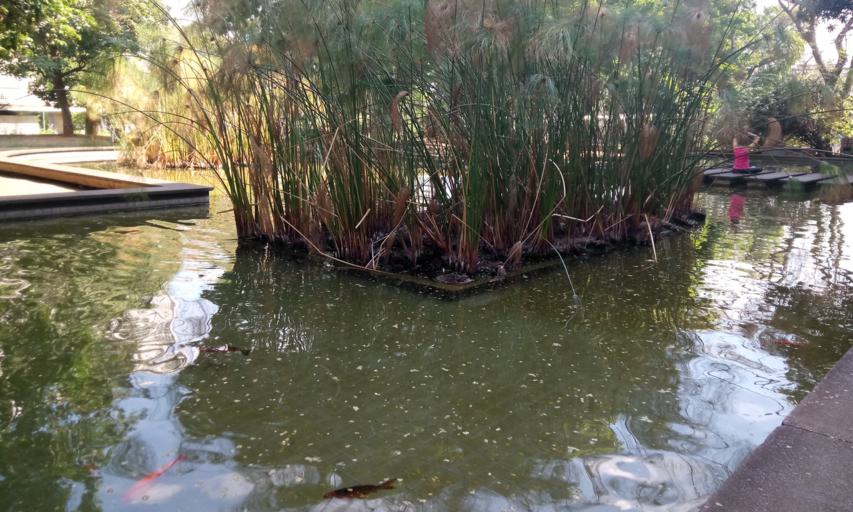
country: BR
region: Federal District
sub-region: Brasilia
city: Brasilia
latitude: -15.8173
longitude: -47.9033
